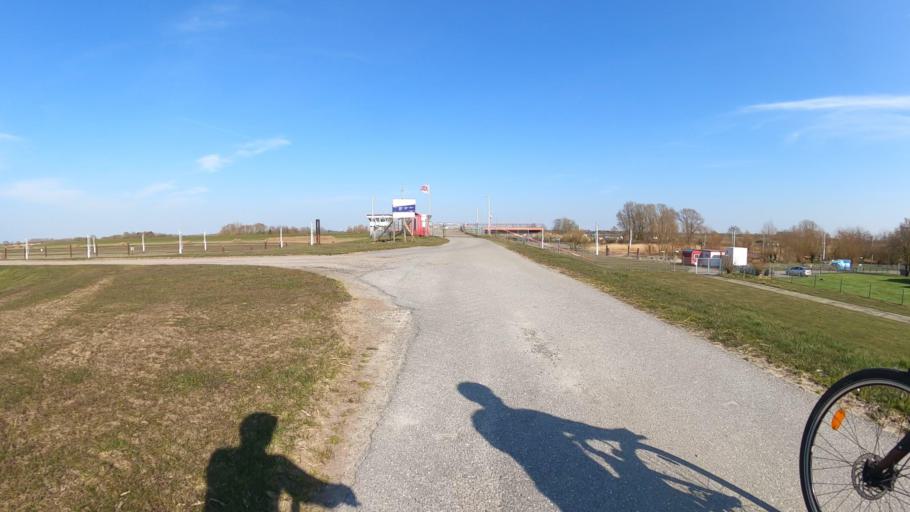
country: DE
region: Schleswig-Holstein
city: Seestermuhe
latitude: 53.6701
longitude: 9.5571
